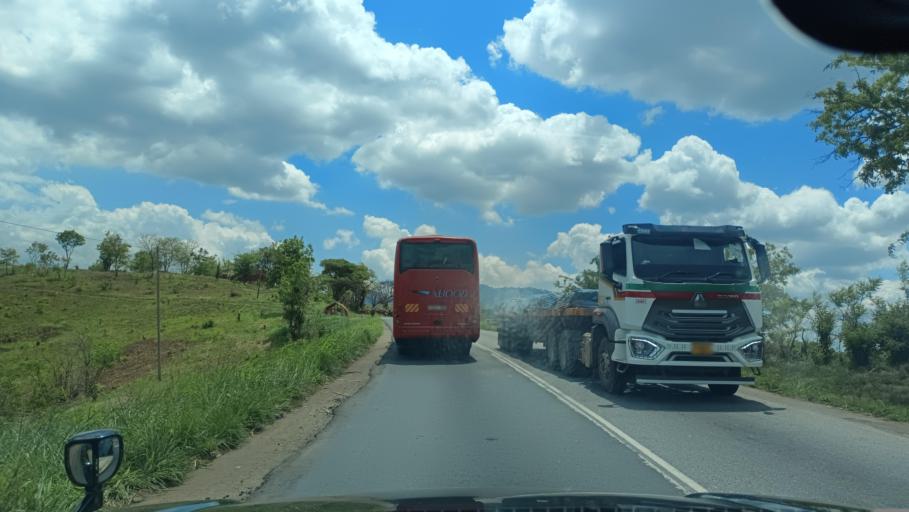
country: TZ
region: Morogoro
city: Mikumi
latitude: -7.4570
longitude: 36.9202
